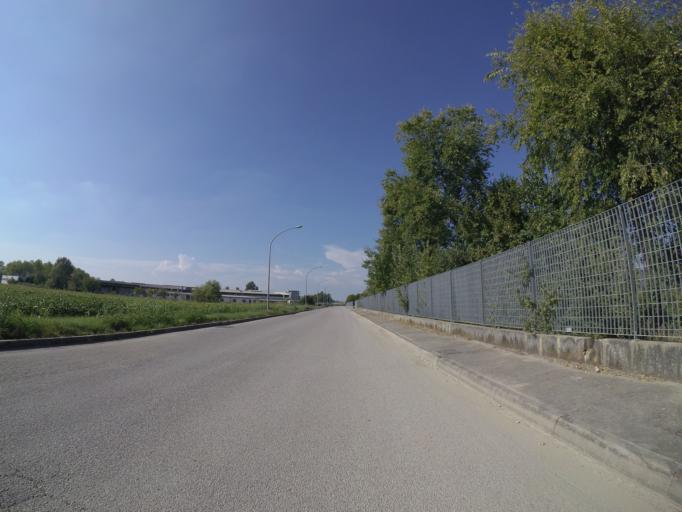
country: IT
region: Friuli Venezia Giulia
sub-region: Provincia di Udine
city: Pocenia
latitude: 45.8314
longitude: 13.1144
